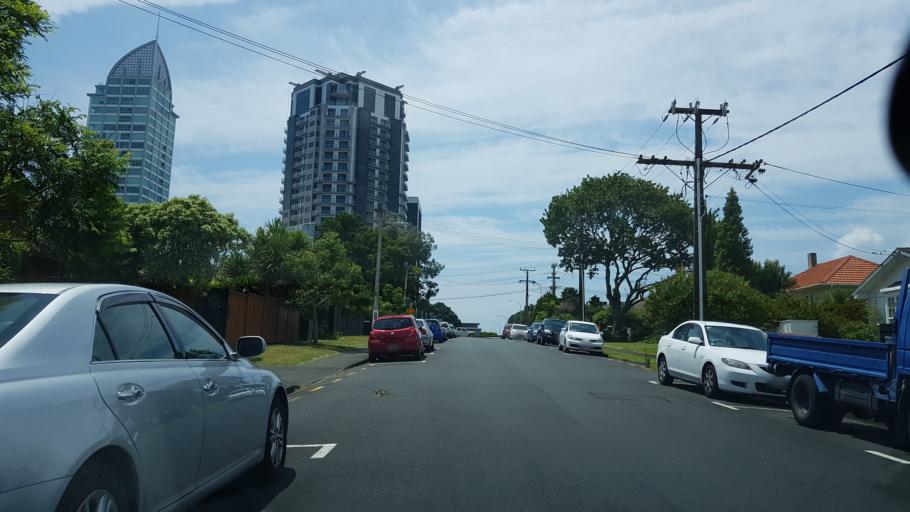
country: NZ
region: Auckland
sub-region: Auckland
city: North Shore
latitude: -36.7919
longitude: 174.7695
